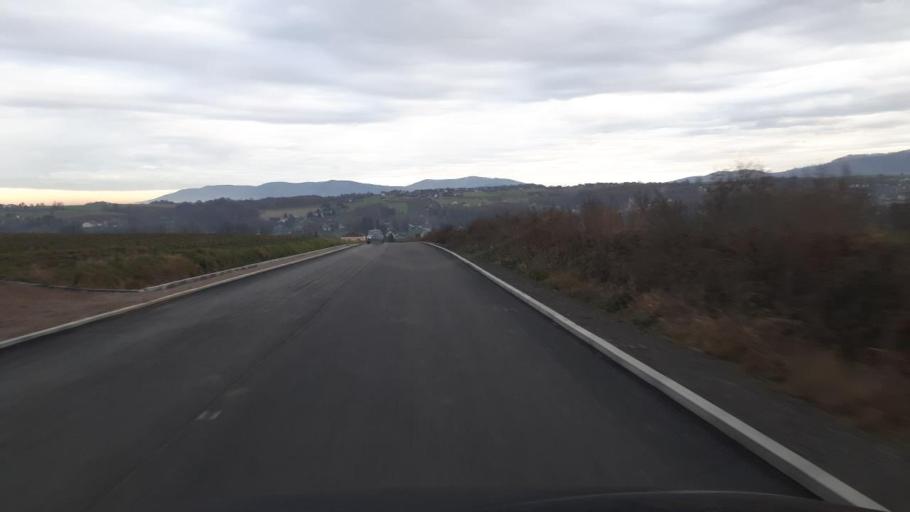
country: PL
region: Silesian Voivodeship
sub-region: Powiat bielski
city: Bronow
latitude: 49.8546
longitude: 18.9289
